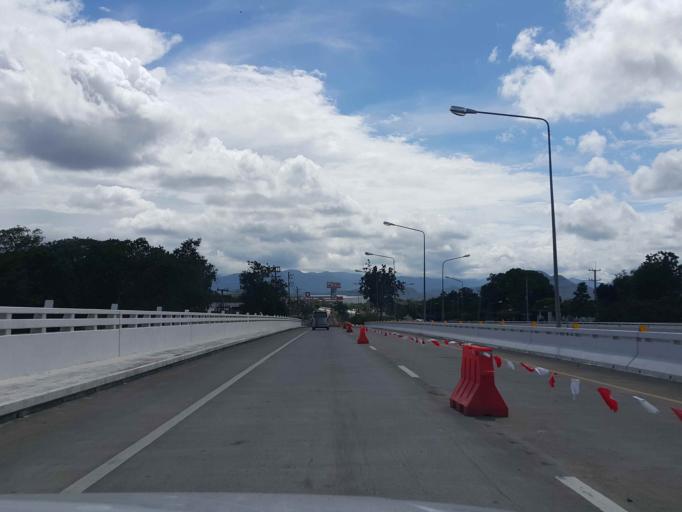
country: TH
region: Tak
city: Tak
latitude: 16.8559
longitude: 99.1235
